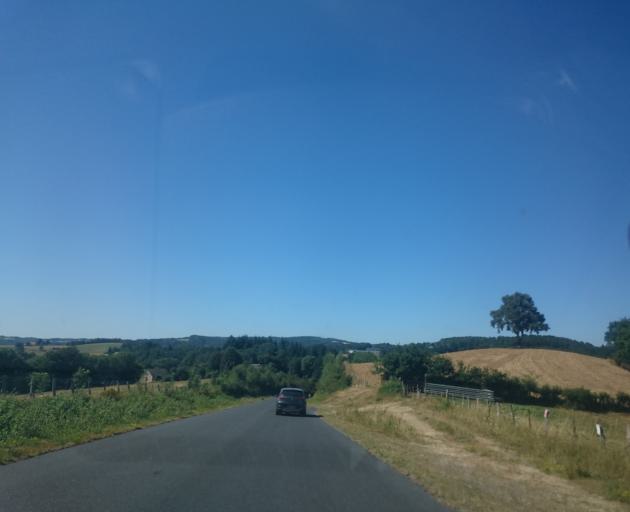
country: FR
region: Auvergne
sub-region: Departement du Cantal
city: Saint-Mamet-la-Salvetat
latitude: 44.7899
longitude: 2.3528
